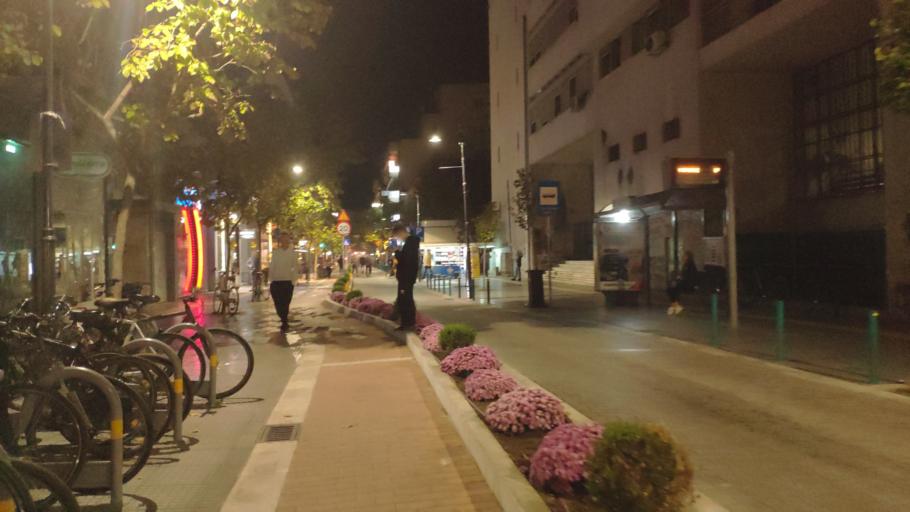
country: GR
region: Thessaly
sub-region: Nomos Larisis
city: Larisa
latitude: 39.6377
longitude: 22.4167
